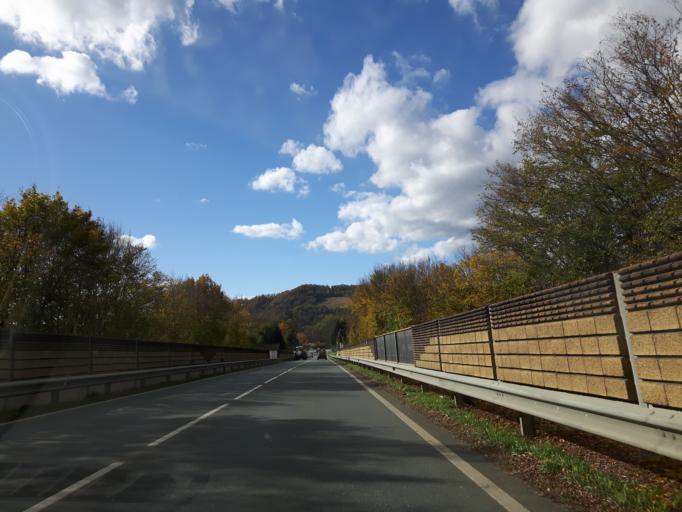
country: AT
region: Styria
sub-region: Politischer Bezirk Leibnitz
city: Kaindorf an der Sulm
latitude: 46.7990
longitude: 15.5417
